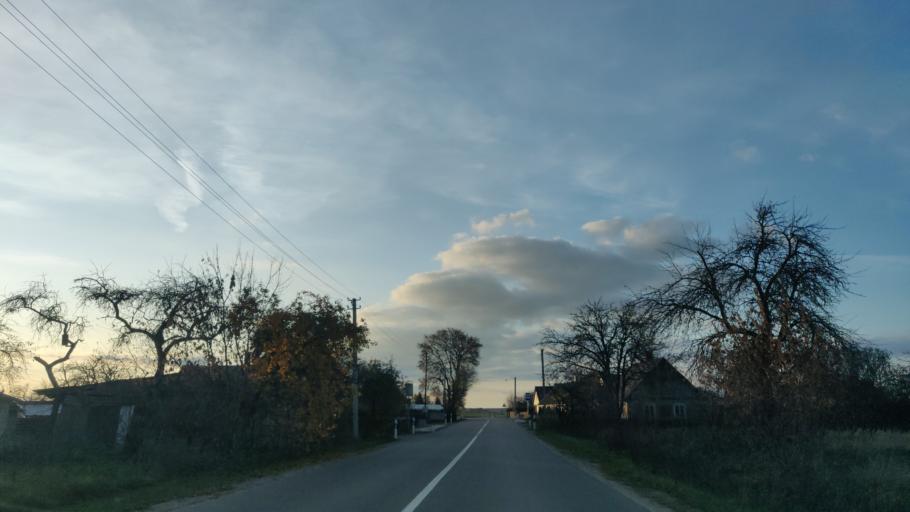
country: LT
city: Lentvaris
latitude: 54.6002
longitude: 25.0189
